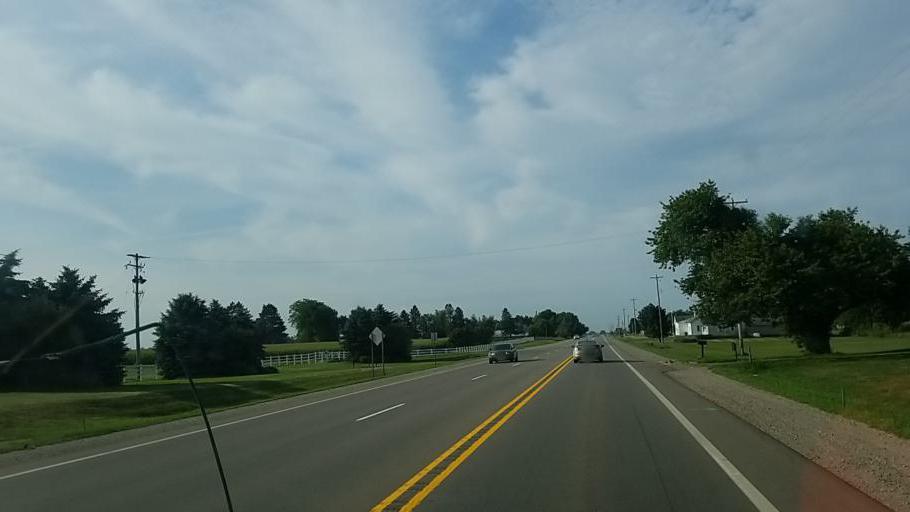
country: US
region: Michigan
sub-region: Ionia County
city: Ionia
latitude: 42.8928
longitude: -85.0750
